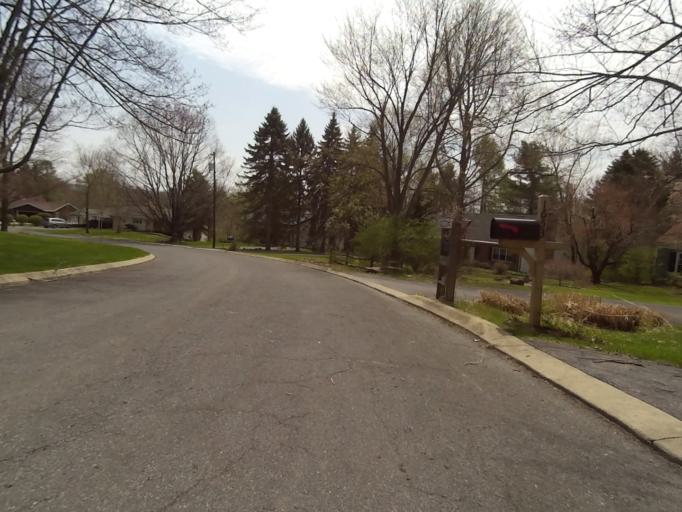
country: US
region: Pennsylvania
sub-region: Centre County
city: Park Forest Village
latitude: 40.7968
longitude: -77.8990
